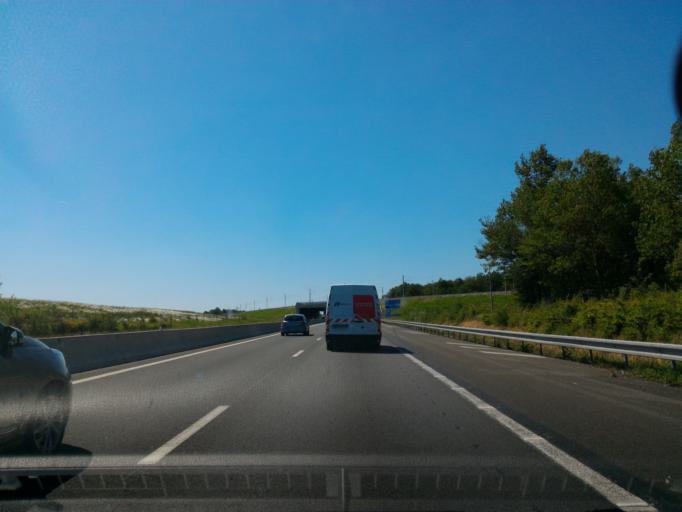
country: FR
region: Centre
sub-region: Departement d'Indre-et-Loire
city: Sorigny
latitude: 47.2281
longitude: 0.6584
